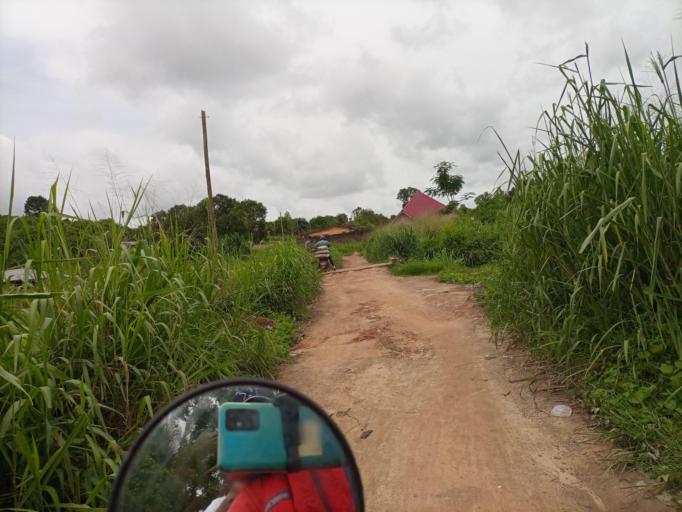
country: SL
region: Southern Province
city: Bo
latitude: 7.9483
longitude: -11.7469
